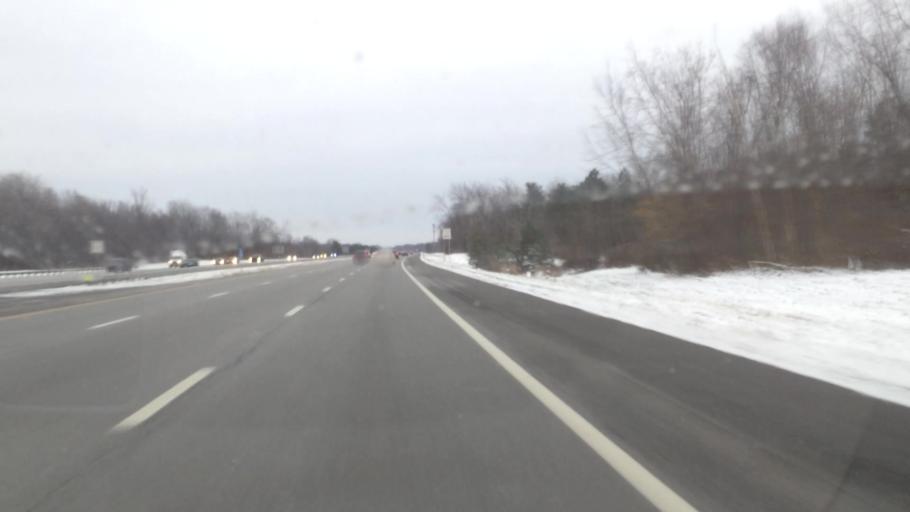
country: US
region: Ohio
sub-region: Cuyahoga County
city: Strongsville
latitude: 41.3025
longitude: -81.8087
